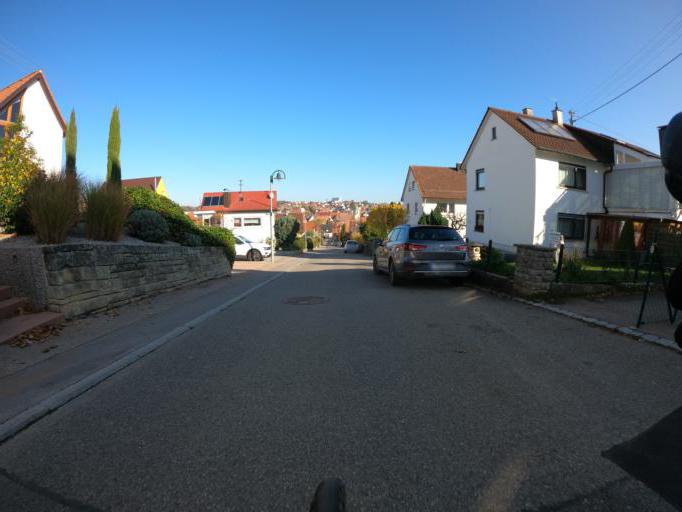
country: DE
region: Baden-Wuerttemberg
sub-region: Regierungsbezirk Stuttgart
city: Weil der Stadt
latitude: 48.7722
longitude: 8.9001
